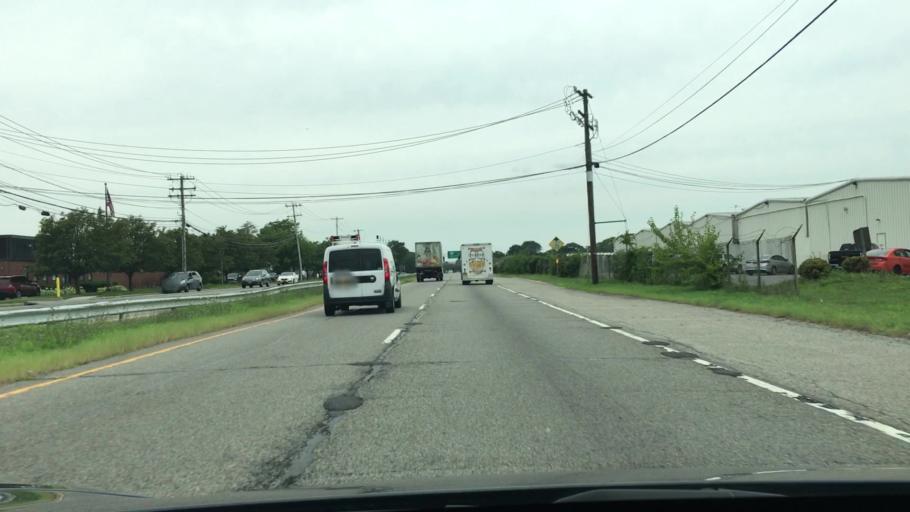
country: US
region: New York
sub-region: Suffolk County
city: East Farmingdale
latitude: 40.7209
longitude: -73.4184
